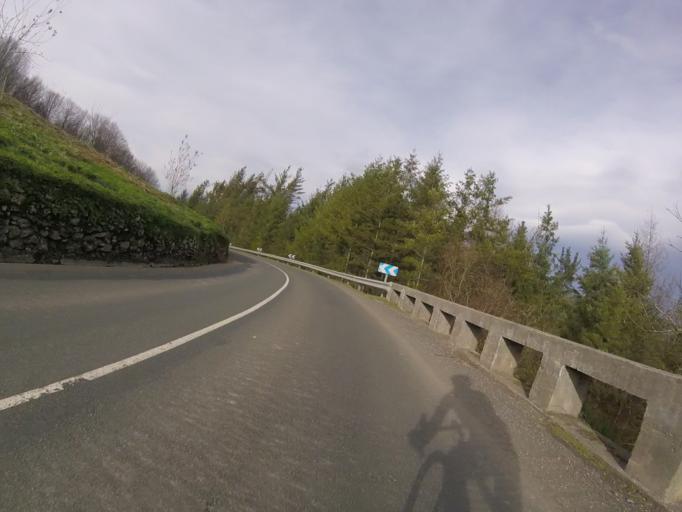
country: ES
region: Basque Country
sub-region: Provincia de Guipuzcoa
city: Beizama
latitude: 43.1682
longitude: -2.2223
